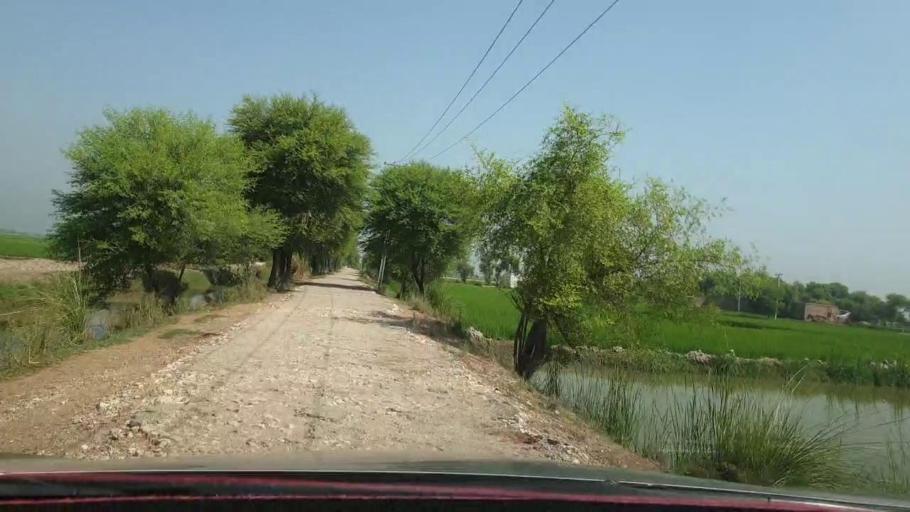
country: PK
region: Sindh
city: Warah
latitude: 27.4961
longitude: 67.8358
